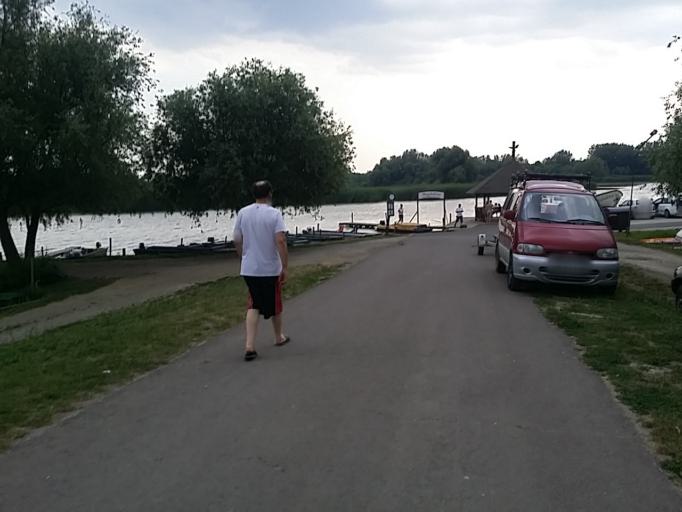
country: HU
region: Heves
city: Poroszlo
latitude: 47.6402
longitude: 20.6535
